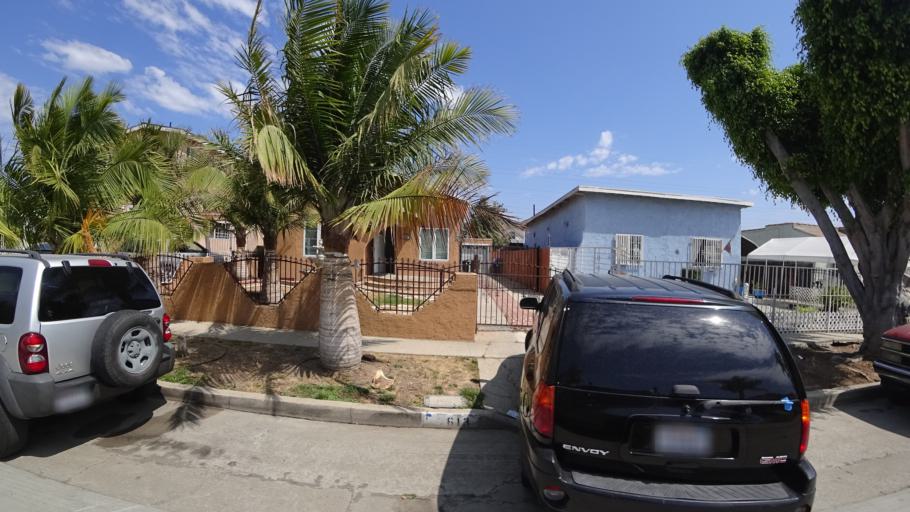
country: US
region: California
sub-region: Los Angeles County
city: Westmont
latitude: 33.9464
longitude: -118.2852
